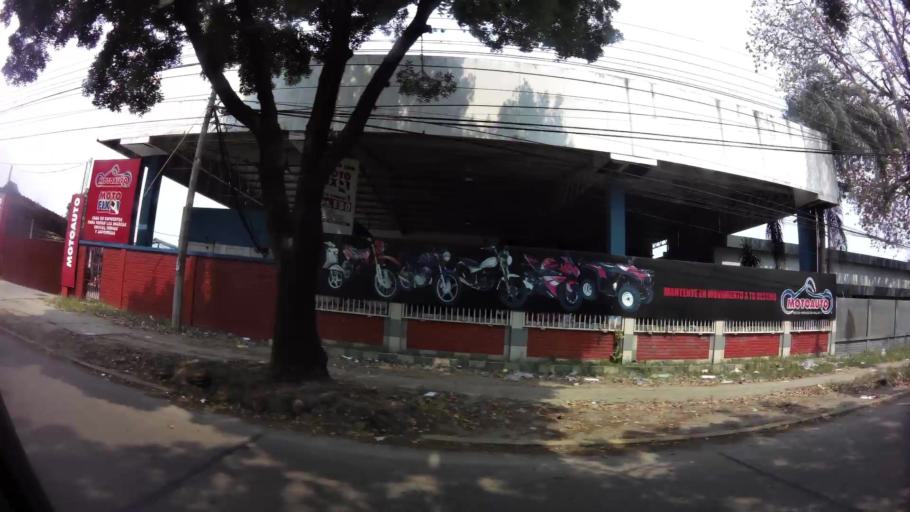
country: HN
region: Cortes
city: San Pedro Sula
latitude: 15.5078
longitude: -88.0129
